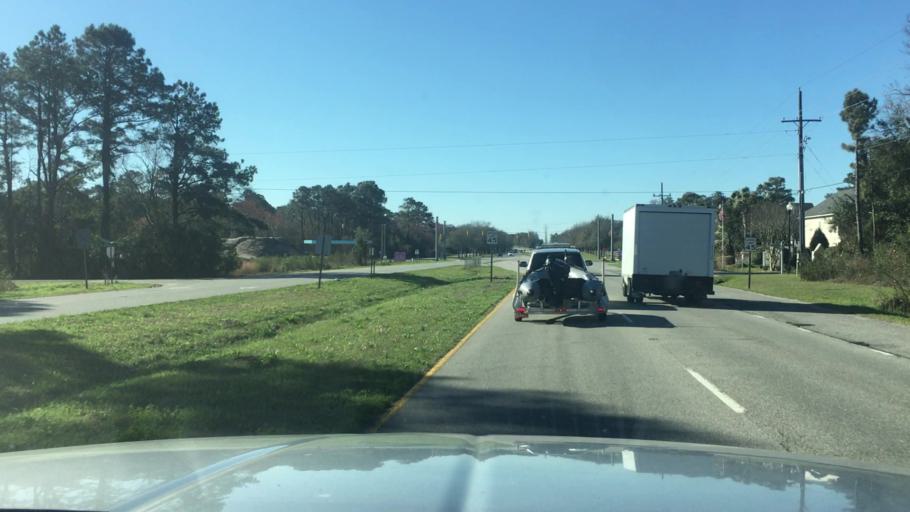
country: US
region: North Carolina
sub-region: New Hanover County
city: Sea Breeze
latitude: 34.0667
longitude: -77.8977
